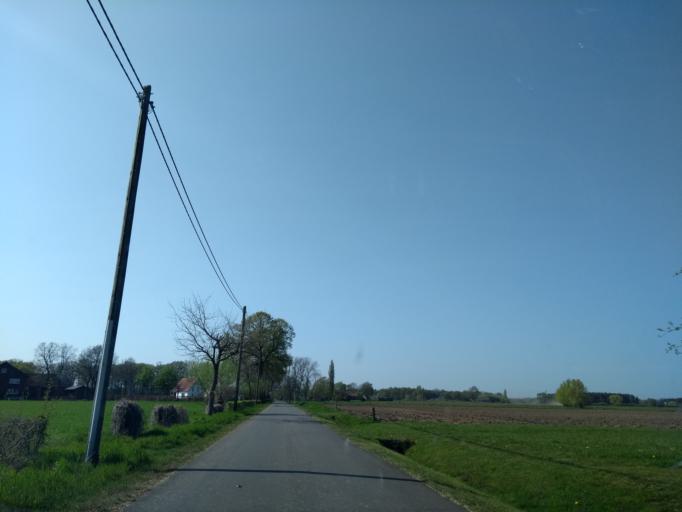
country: DE
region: North Rhine-Westphalia
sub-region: Regierungsbezirk Detmold
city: Delbruck
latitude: 51.7075
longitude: 8.5372
